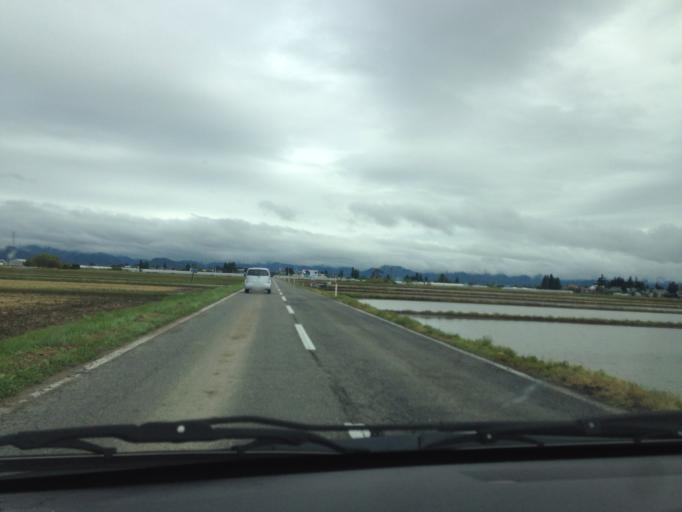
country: JP
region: Fukushima
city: Kitakata
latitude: 37.5255
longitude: 139.8616
